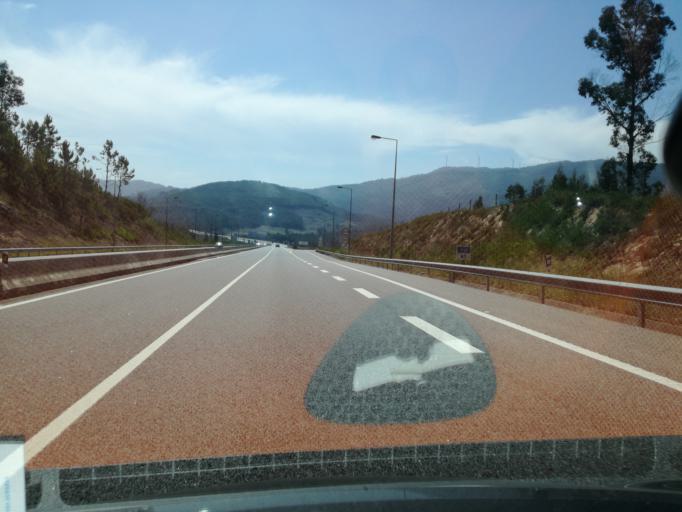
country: PT
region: Viana do Castelo
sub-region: Caminha
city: Vila Praia de Ancora
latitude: 41.8091
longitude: -8.8047
